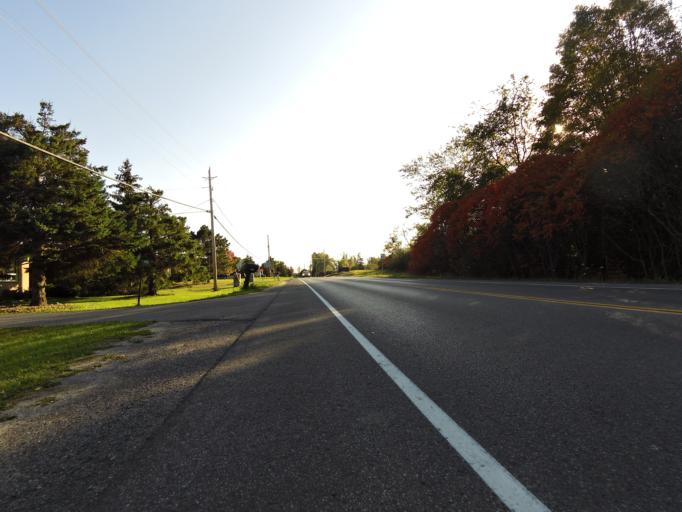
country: CA
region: Ontario
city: Kingston
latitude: 44.3161
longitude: -76.4637
